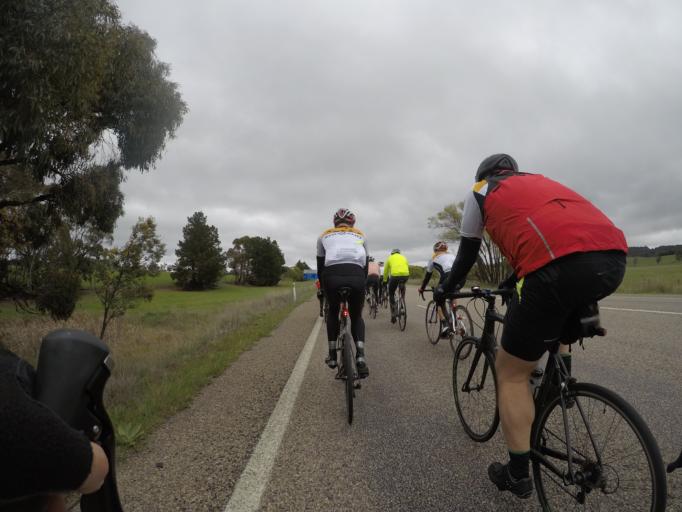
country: AU
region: New South Wales
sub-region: Lithgow
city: Portland
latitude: -33.4332
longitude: 149.9067
